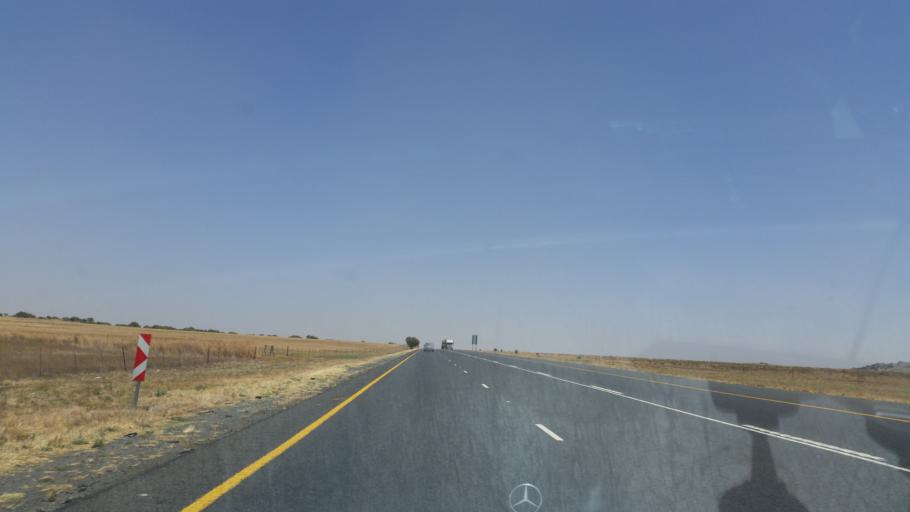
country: ZA
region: Orange Free State
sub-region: Lejweleputswa District Municipality
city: Winburg
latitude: -28.6971
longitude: 26.8045
